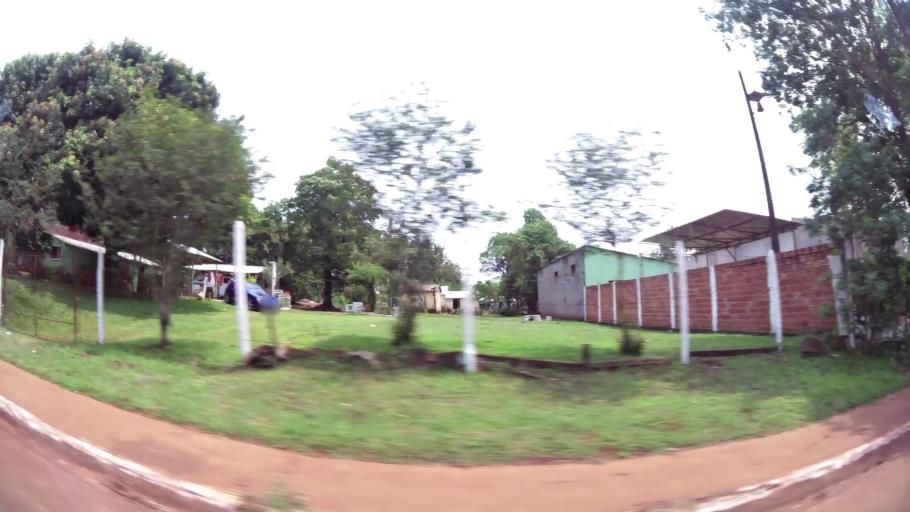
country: BR
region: Parana
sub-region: Foz Do Iguacu
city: Foz do Iguacu
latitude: -25.5713
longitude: -54.6056
